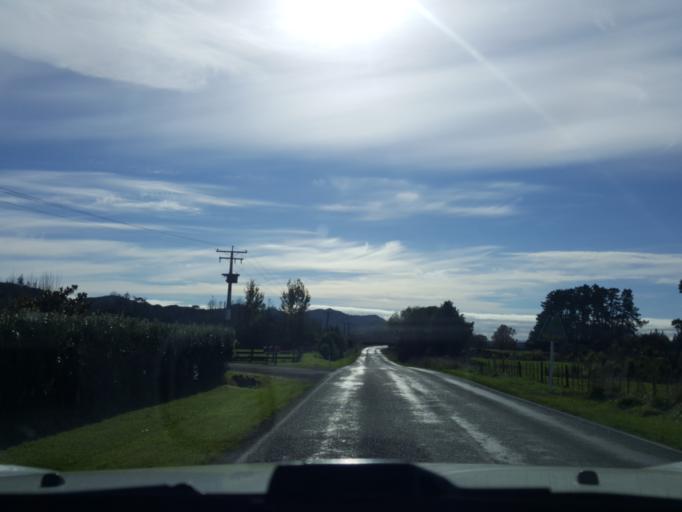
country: NZ
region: Waikato
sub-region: Waikato District
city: Ngaruawahia
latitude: -37.6080
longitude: 175.1976
